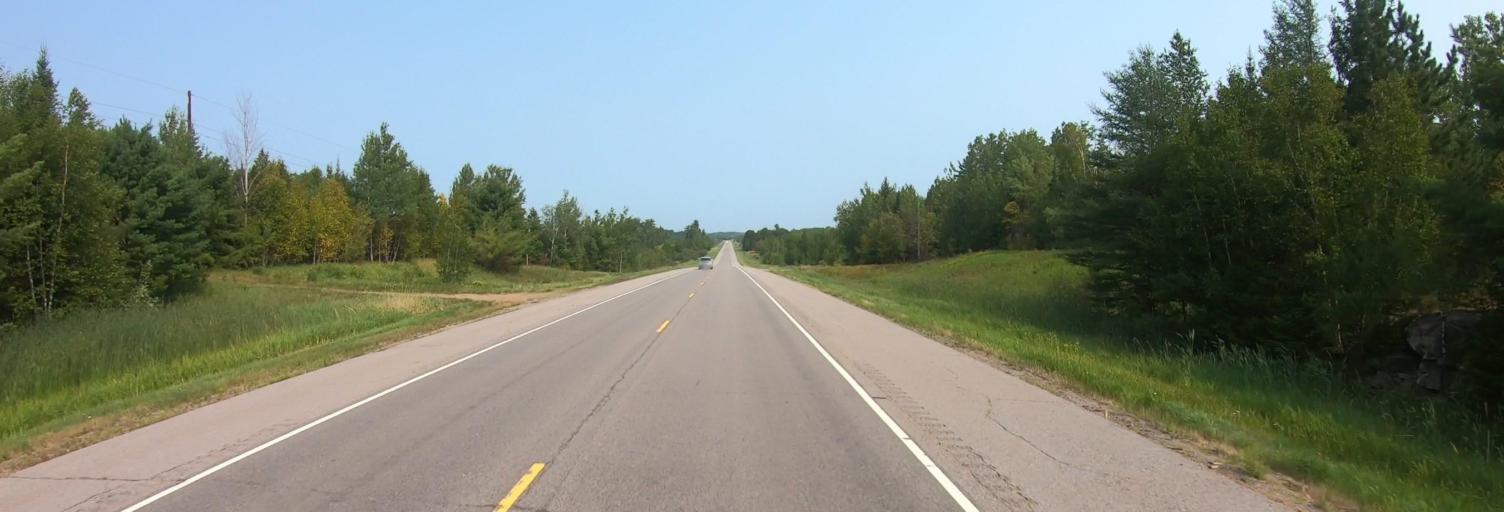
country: US
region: Minnesota
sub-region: Saint Louis County
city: Mountain Iron
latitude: 48.0051
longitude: -92.8307
